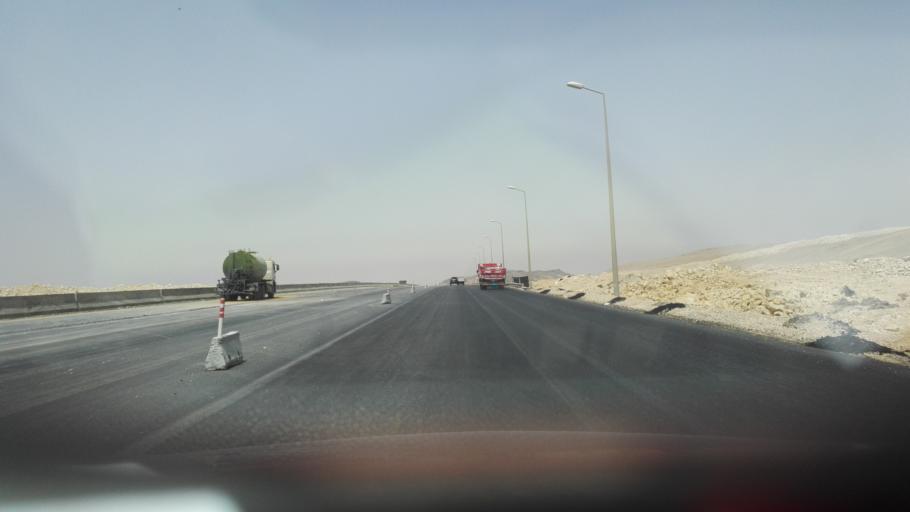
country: EG
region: As Suways
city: Ain Sukhna
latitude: 29.7020
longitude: 32.0960
